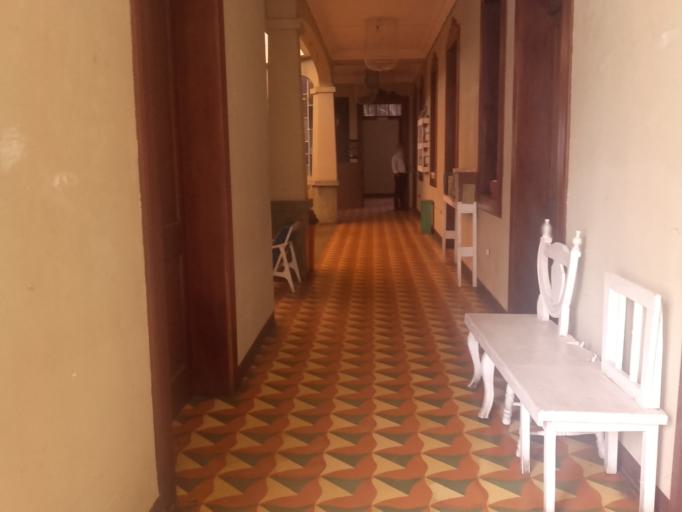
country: GT
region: Guatemala
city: Guatemala City
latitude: 14.6465
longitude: -90.5155
